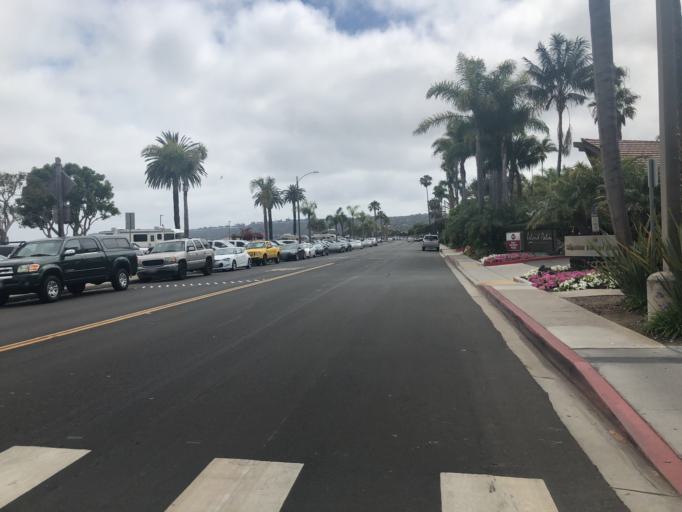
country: US
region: California
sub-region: San Diego County
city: Coronado
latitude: 32.7139
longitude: -117.2266
